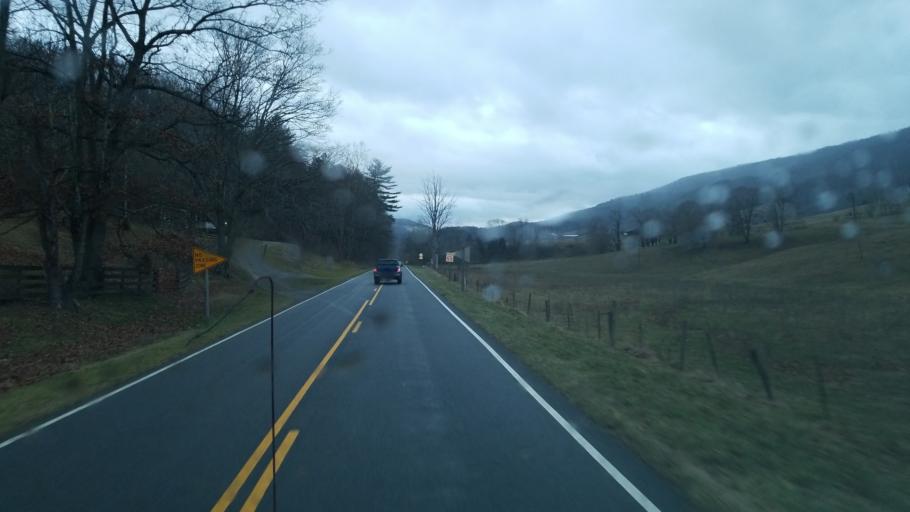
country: US
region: Virginia
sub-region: Giles County
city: Narrows
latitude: 37.2031
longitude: -80.8188
